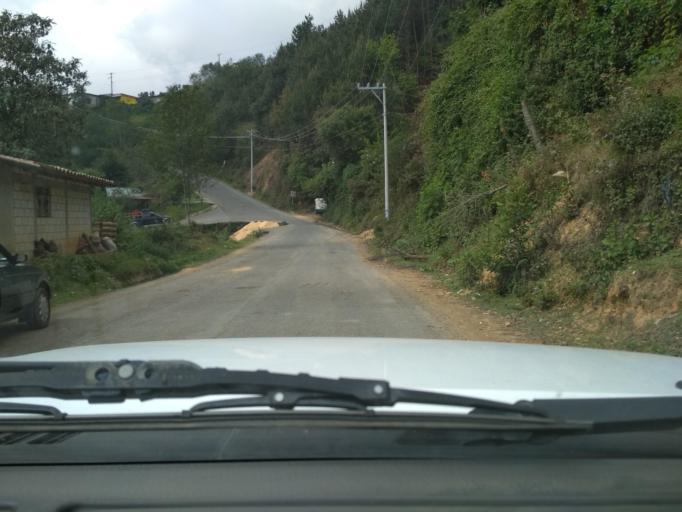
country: MX
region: Veracruz
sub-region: Camerino Z. Mendoza
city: Necoxtla
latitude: 18.7698
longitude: -97.1522
